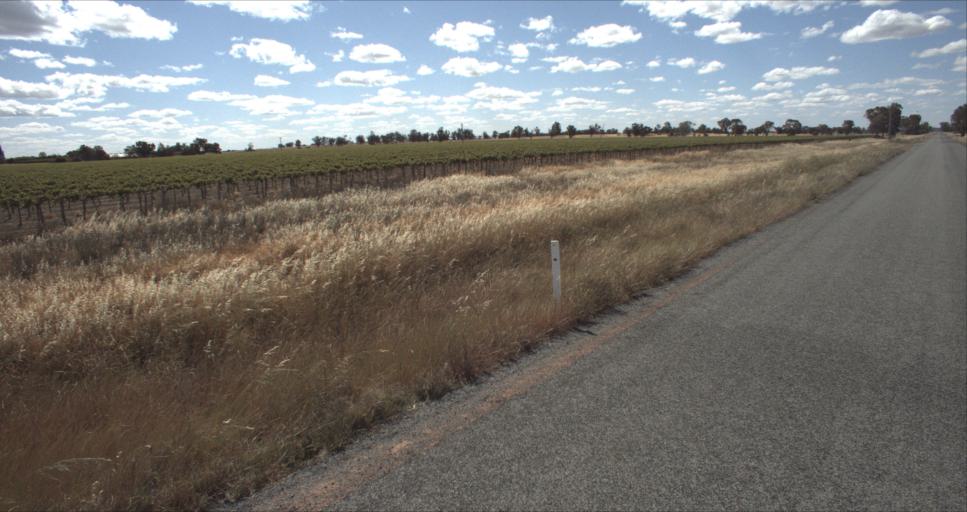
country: AU
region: New South Wales
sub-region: Leeton
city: Leeton
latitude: -34.4962
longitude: 146.2463
